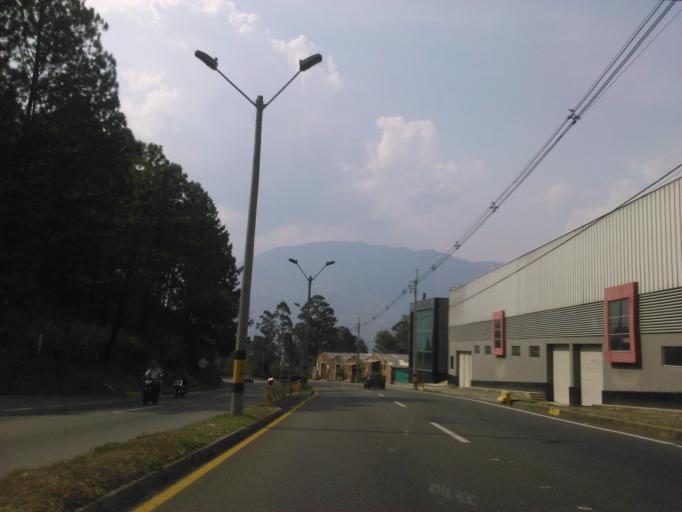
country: CO
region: Antioquia
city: Bello
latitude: 6.3187
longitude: -75.5320
